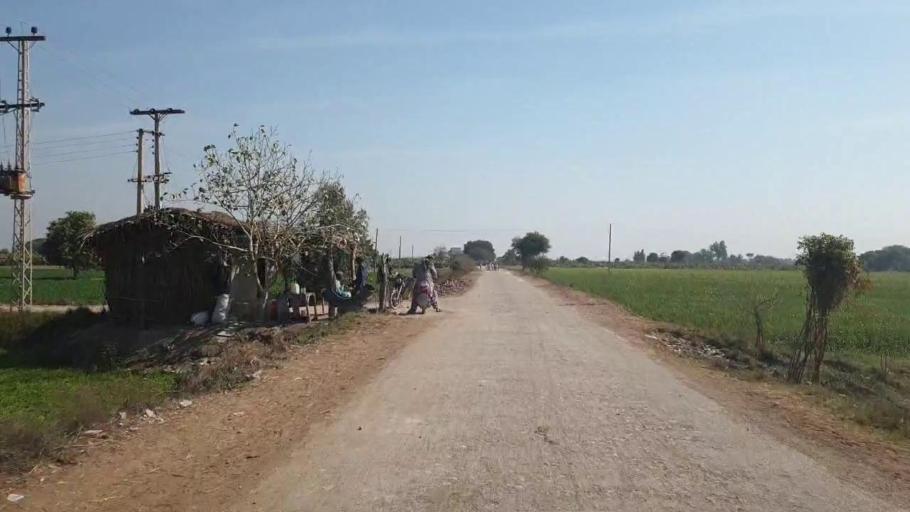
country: PK
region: Sindh
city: Chambar
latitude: 25.3857
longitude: 68.7926
